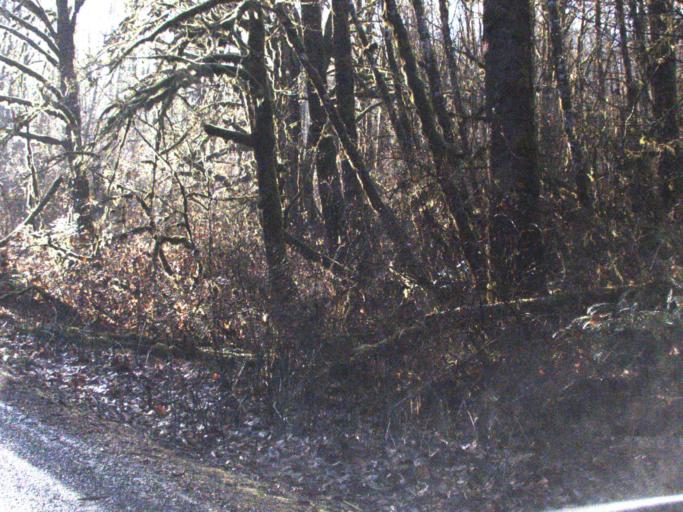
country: US
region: Washington
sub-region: Snohomish County
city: Darrington
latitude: 48.4648
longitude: -121.5866
